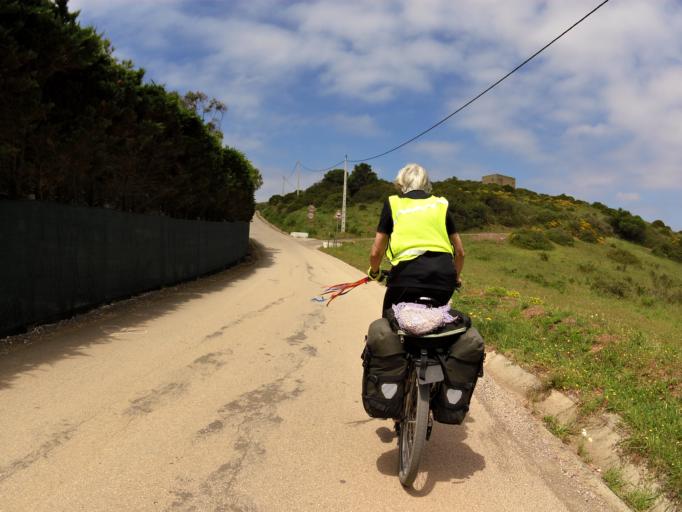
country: PT
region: Faro
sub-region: Vila do Bispo
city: Vila do Bispo
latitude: 37.0675
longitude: -8.8586
